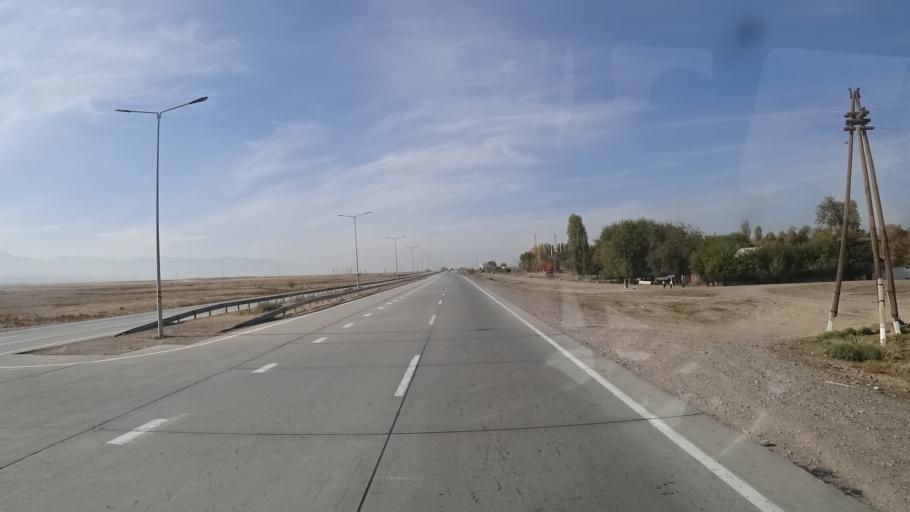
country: KZ
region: Zhambyl
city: Merke
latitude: 42.8886
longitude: 72.9945
